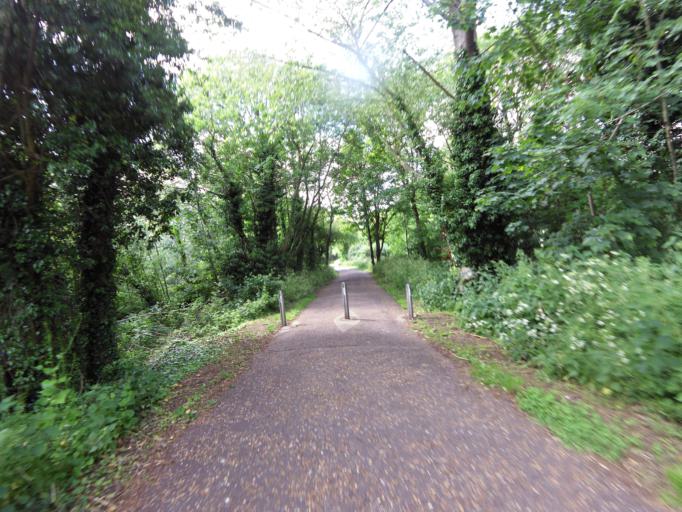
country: GB
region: England
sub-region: Norfolk
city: Norwich
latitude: 52.6416
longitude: 1.2814
